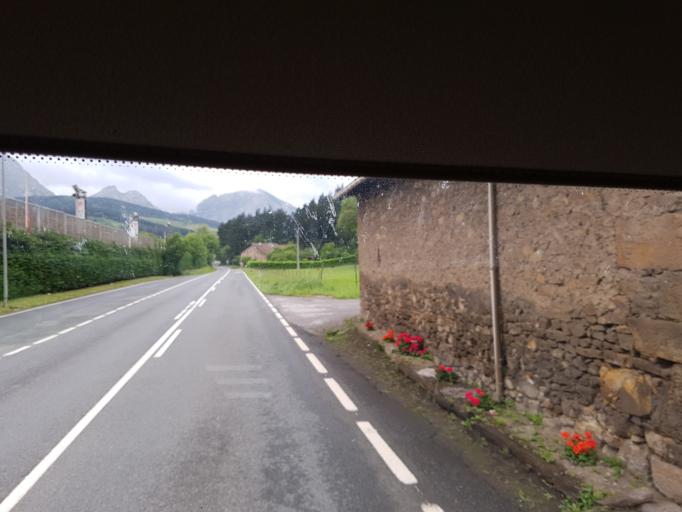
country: ES
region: Basque Country
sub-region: Bizkaia
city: Elorrio
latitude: 43.1305
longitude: -2.5728
